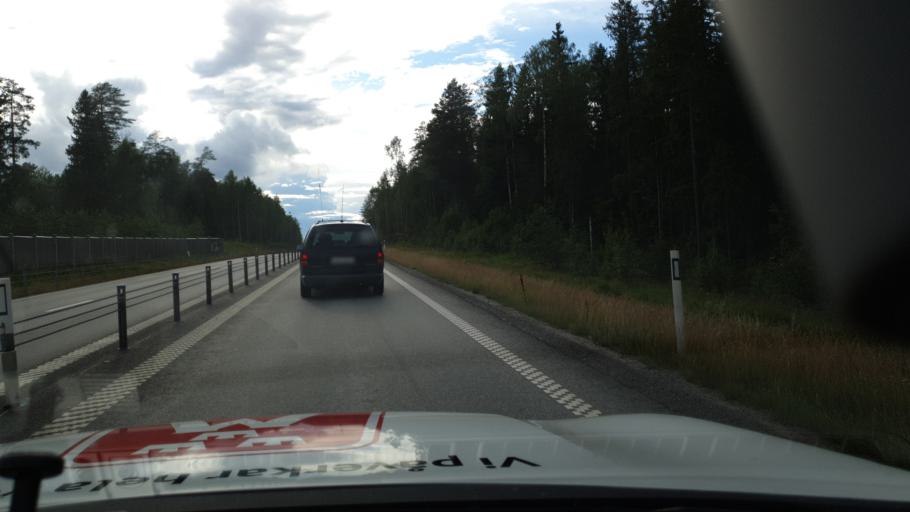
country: SE
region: Vaesterbotten
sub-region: Umea Kommun
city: Ersmark
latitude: 63.8479
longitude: 20.3352
